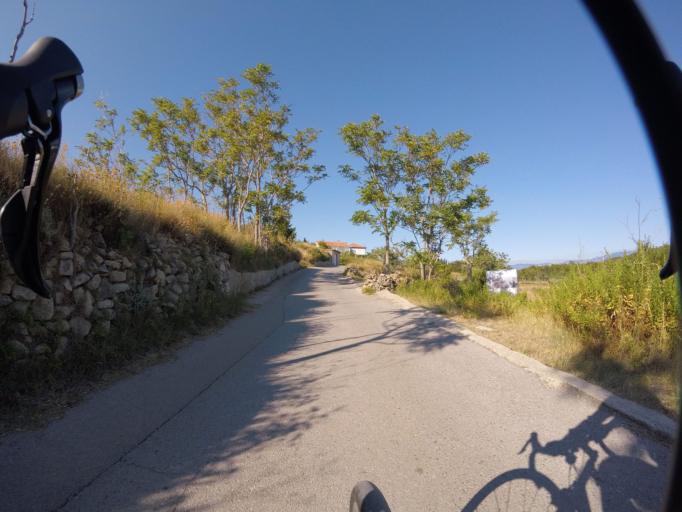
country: HR
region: Primorsko-Goranska
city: Lopar
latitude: 44.8361
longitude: 14.7367
